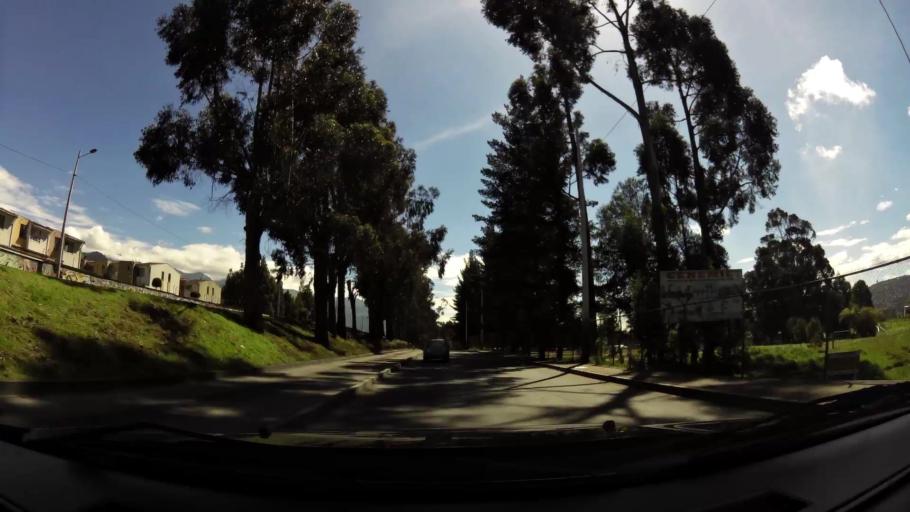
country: EC
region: Pichincha
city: Quito
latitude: -0.2907
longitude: -78.5578
